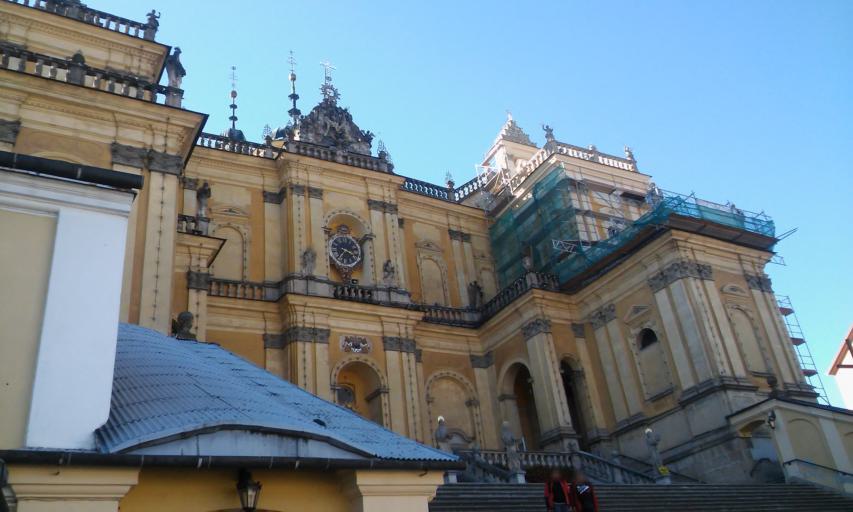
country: PL
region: Lower Silesian Voivodeship
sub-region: Powiat klodzki
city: Radkow
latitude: 50.4900
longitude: 16.4554
